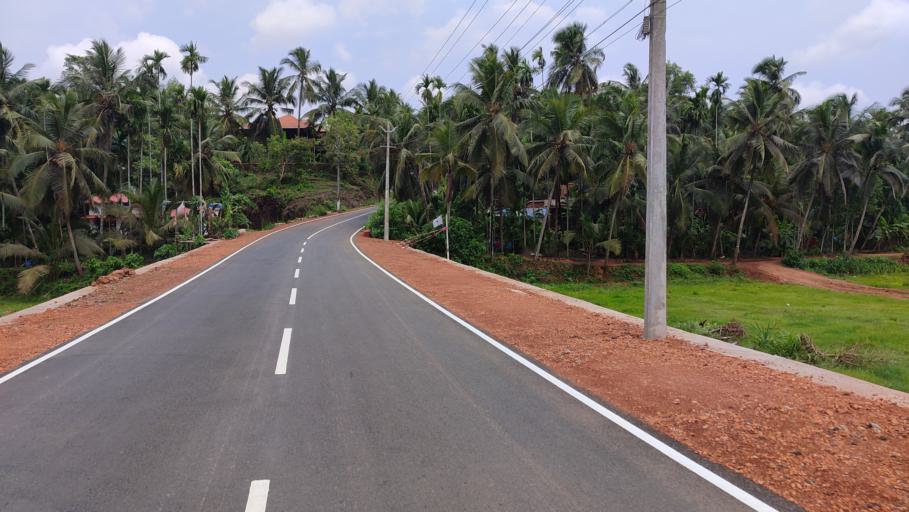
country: IN
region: Kerala
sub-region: Kasaragod District
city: Kannangad
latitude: 12.3167
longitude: 75.1378
